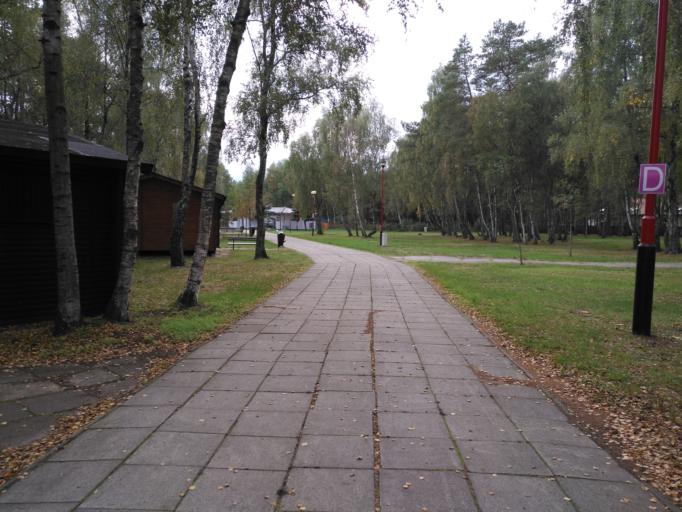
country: PL
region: West Pomeranian Voivodeship
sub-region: Powiat kolobrzeski
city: Grzybowo
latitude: 54.1612
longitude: 15.4246
